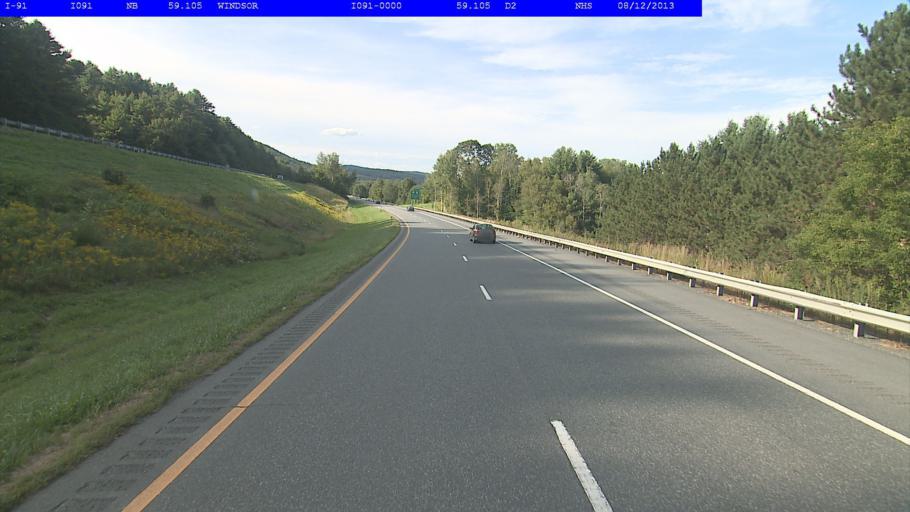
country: US
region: Vermont
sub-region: Windsor County
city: Windsor
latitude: 43.5099
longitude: -72.4059
